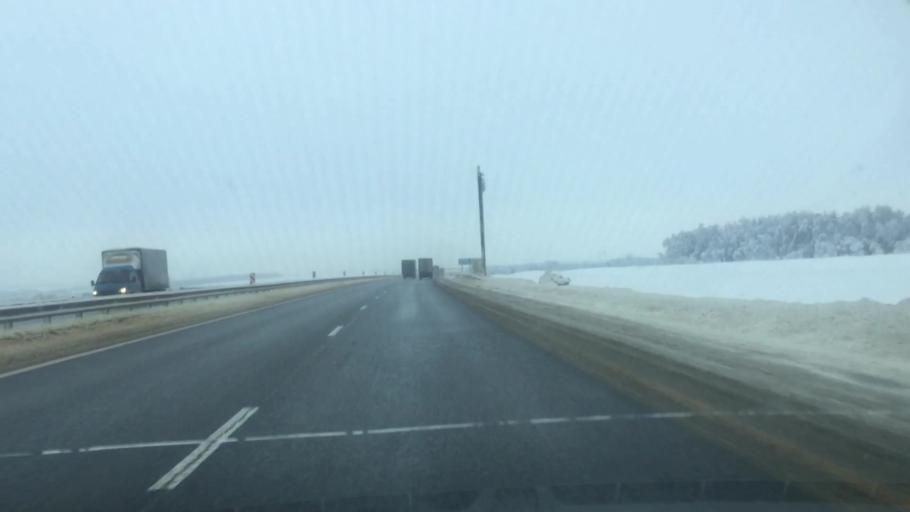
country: RU
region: Lipetsk
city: Stanovoye
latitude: 52.7426
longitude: 38.4729
